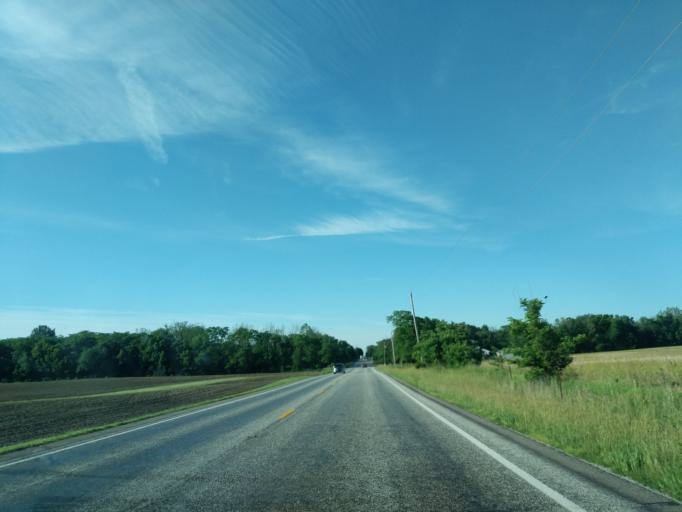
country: US
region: Indiana
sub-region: Madison County
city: Ingalls
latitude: 39.9130
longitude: -85.7709
